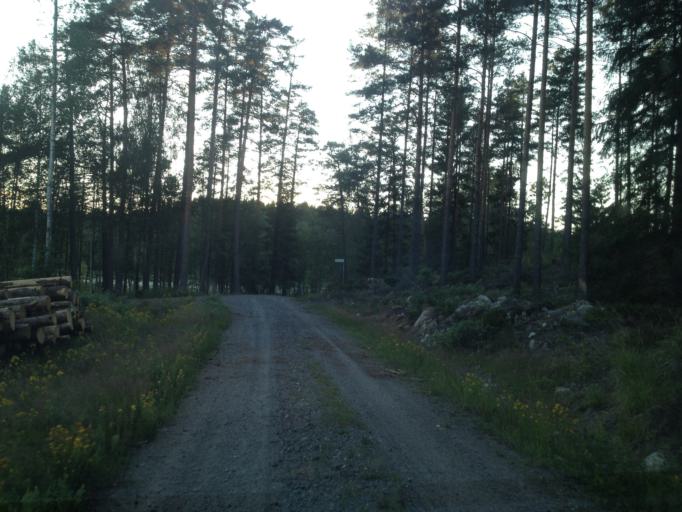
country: SE
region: Kalmar
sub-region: Vasterviks Kommun
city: Overum
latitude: 58.0016
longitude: 16.1234
